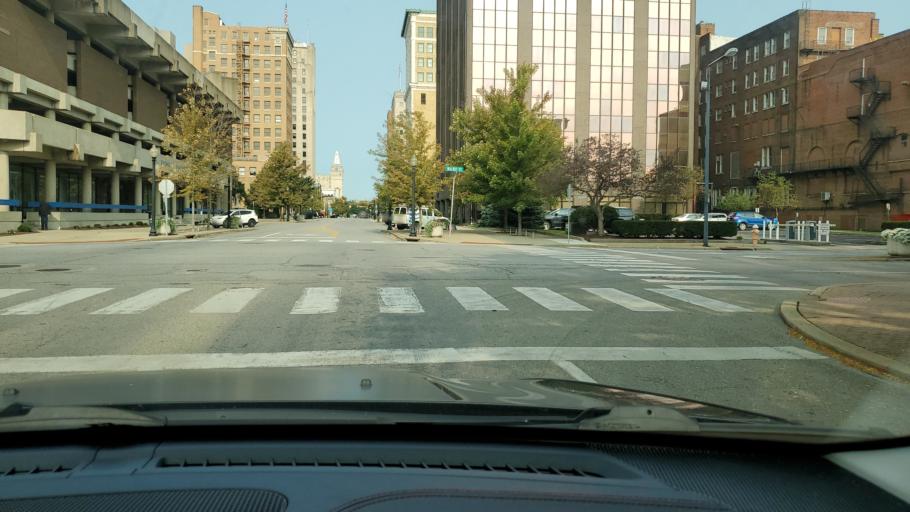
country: US
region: Ohio
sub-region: Mahoning County
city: Youngstown
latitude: 41.0990
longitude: -80.6468
